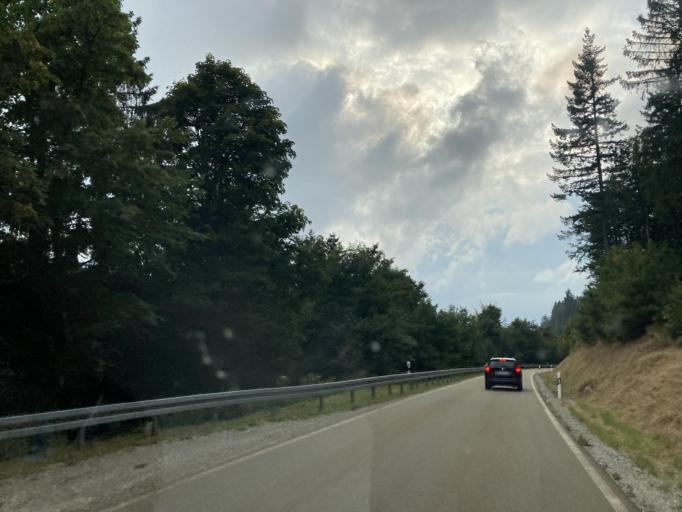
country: DE
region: Baden-Wuerttemberg
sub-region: Freiburg Region
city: Muenstertal/Schwarzwald
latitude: 47.7978
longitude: 7.7630
